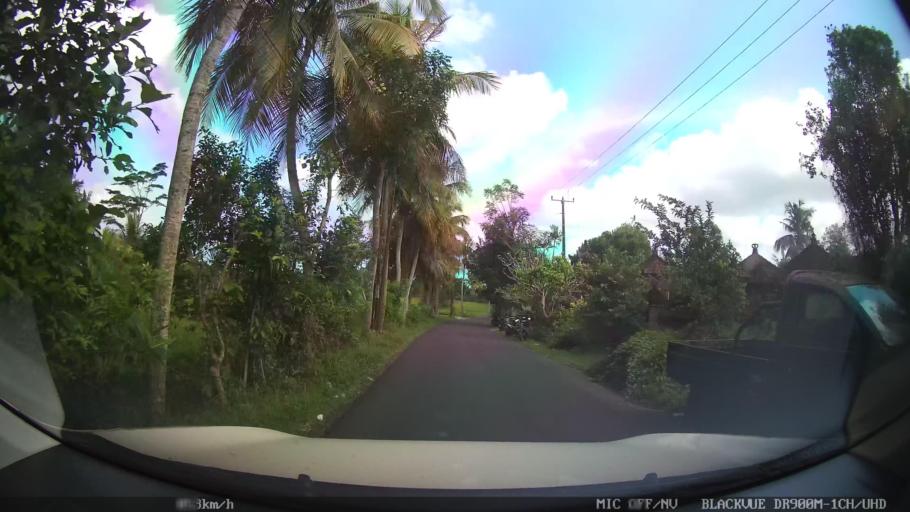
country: ID
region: Bali
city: Banjar Mulung
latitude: -8.5014
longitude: 115.3221
